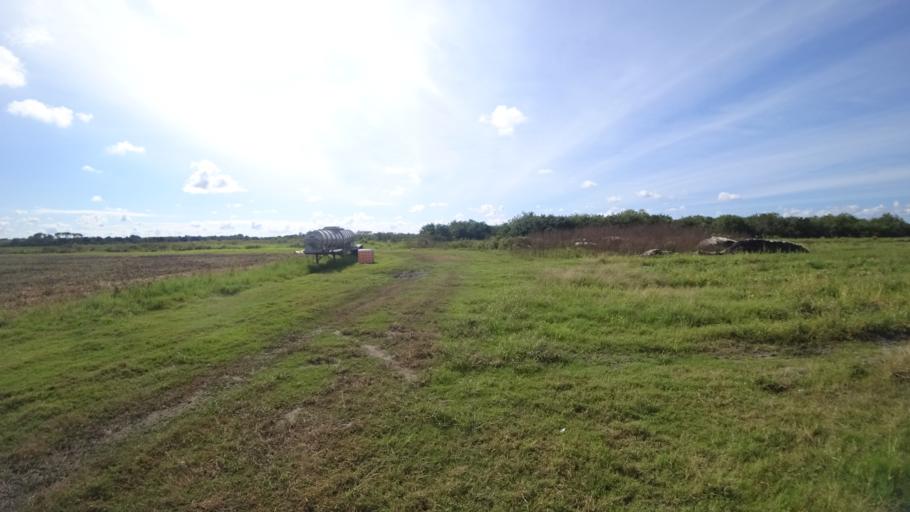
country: US
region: Florida
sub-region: Sarasota County
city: The Meadows
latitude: 27.4445
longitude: -82.3201
